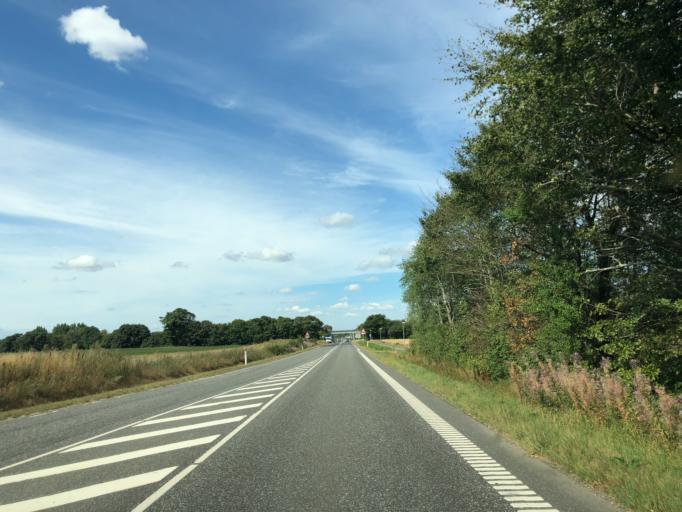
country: DK
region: Central Jutland
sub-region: Ikast-Brande Kommune
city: Bording Kirkeby
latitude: 56.1373
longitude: 9.3570
